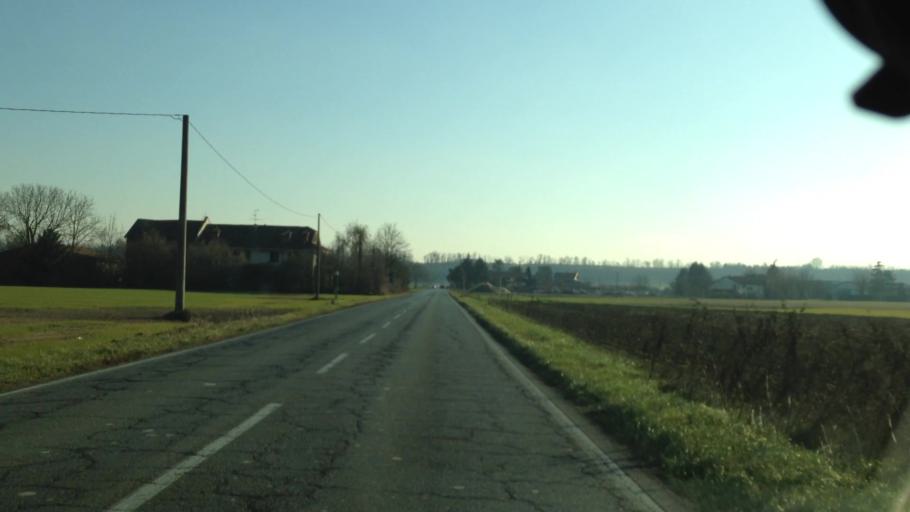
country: IT
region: Piedmont
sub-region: Provincia di Alessandria
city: Felizzano
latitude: 44.8816
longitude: 8.4429
